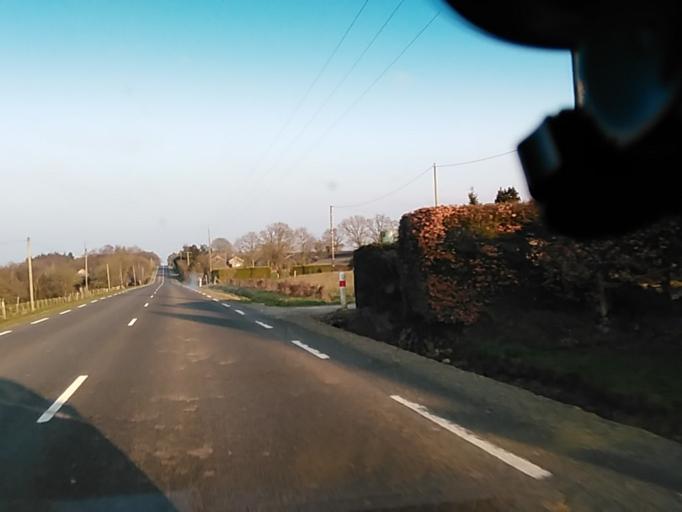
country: FR
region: Lower Normandy
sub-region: Departement de l'Orne
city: Domfront
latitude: 48.5943
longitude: -0.6030
